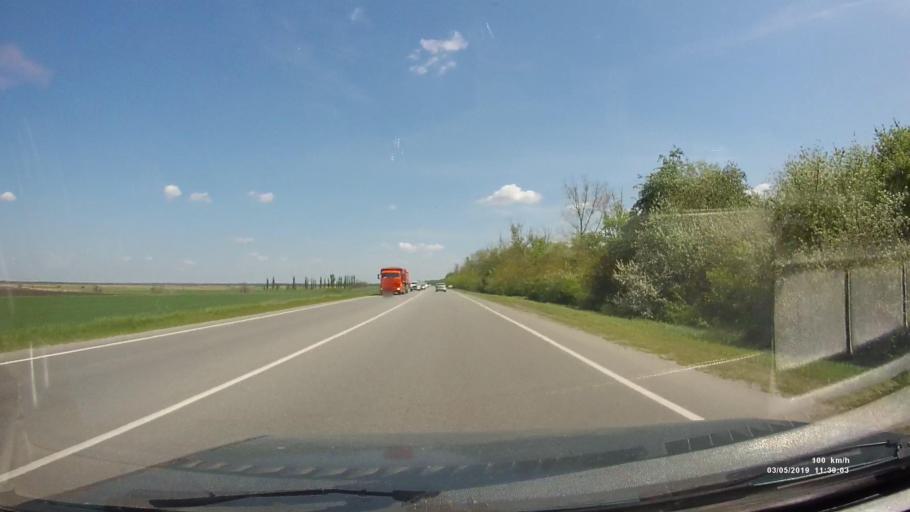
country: RU
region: Rostov
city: Ol'ginskaya
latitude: 47.1316
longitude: 39.9784
